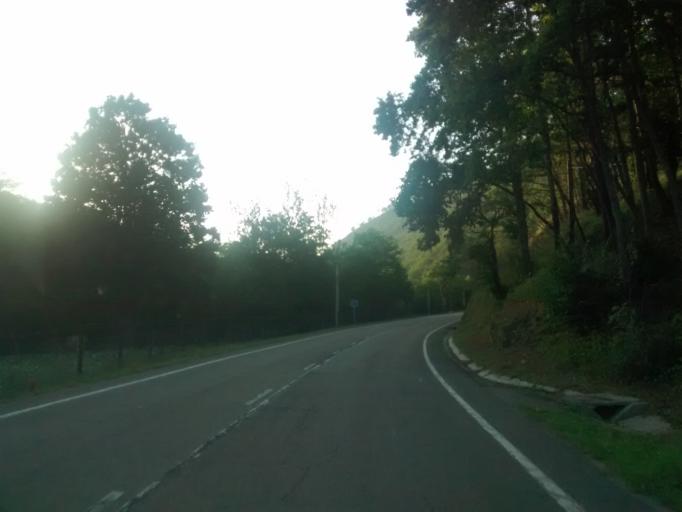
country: ES
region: Cantabria
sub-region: Provincia de Cantabria
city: Ruente
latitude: 43.1495
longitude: -4.2168
